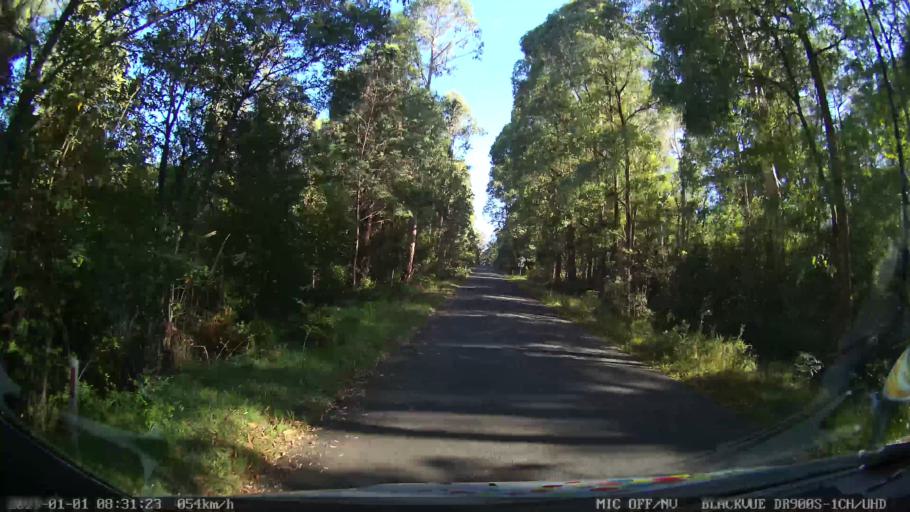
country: AU
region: New South Wales
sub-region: Snowy River
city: Jindabyne
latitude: -36.3708
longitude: 148.2050
